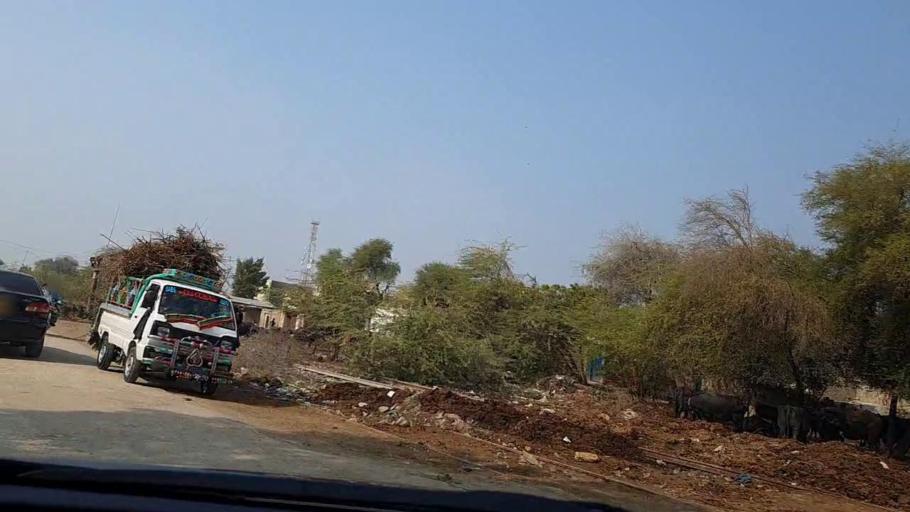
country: PK
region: Sindh
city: Sakrand
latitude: 26.1428
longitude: 68.2725
